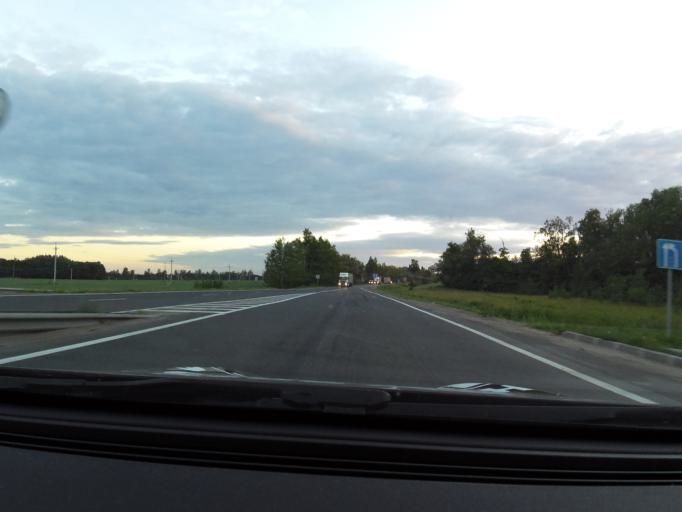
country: RU
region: Chuvashia
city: Yadrin
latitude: 56.0416
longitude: 46.2948
